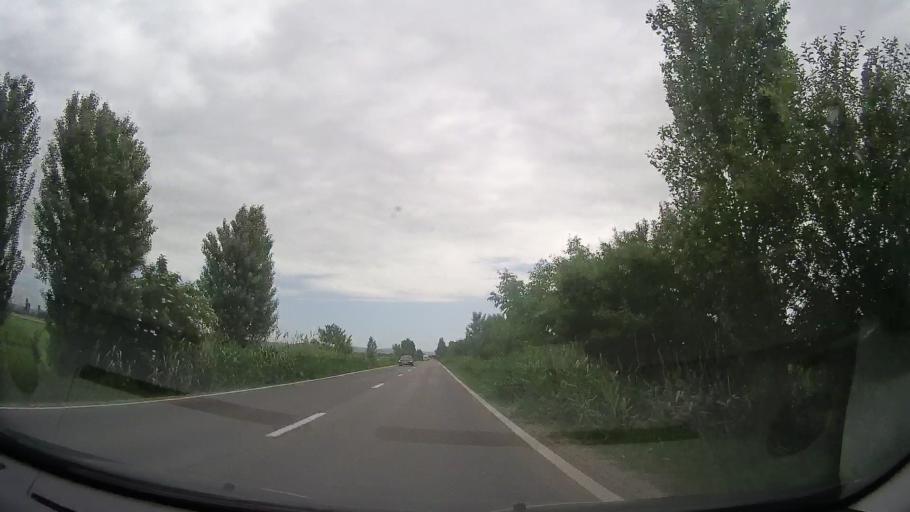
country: RO
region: Prahova
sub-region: Comuna Berceni
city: Corlatesti
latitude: 44.9048
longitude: 26.0718
